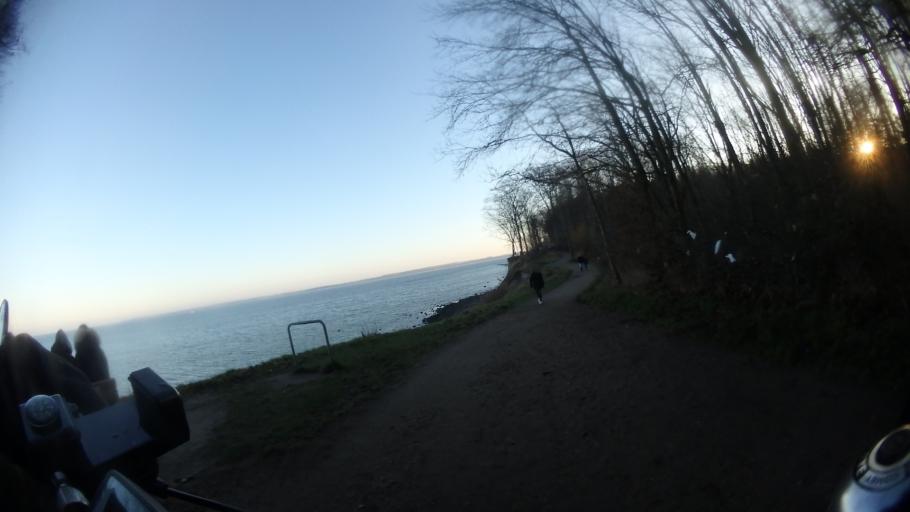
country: DE
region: Schleswig-Holstein
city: Travemuende
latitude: 53.9854
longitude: 10.8781
